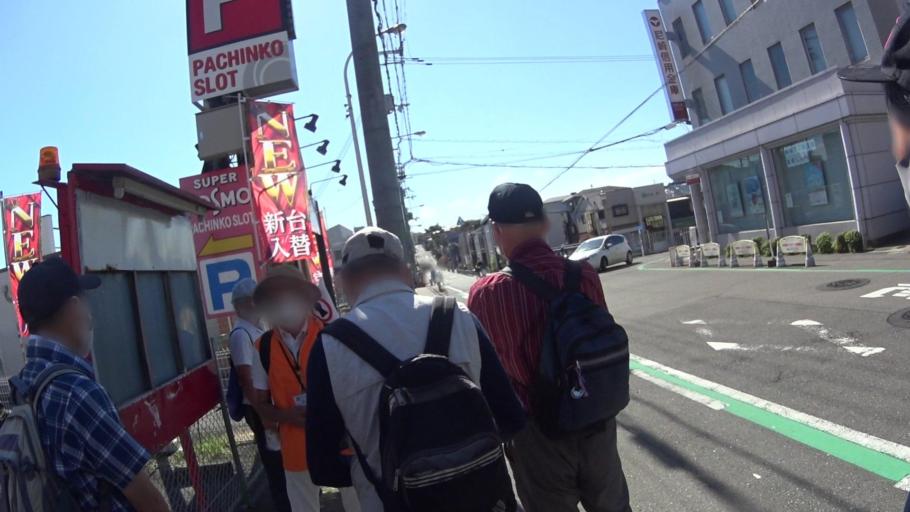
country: JP
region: Osaka
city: Takaishi
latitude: 34.5039
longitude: 135.4421
